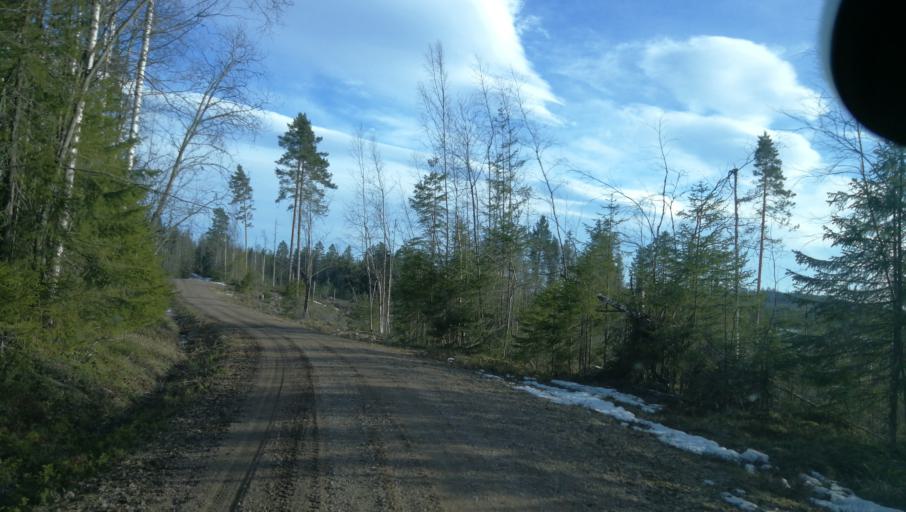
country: SE
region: Dalarna
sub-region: Vansbro Kommun
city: Vansbro
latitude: 60.8015
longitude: 14.2132
